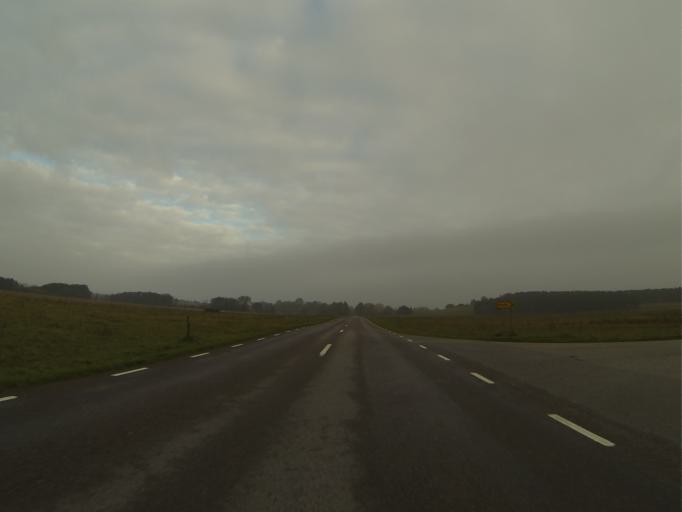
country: SE
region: Skane
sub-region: Lunds Kommun
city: Veberod
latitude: 55.6768
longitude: 13.4987
